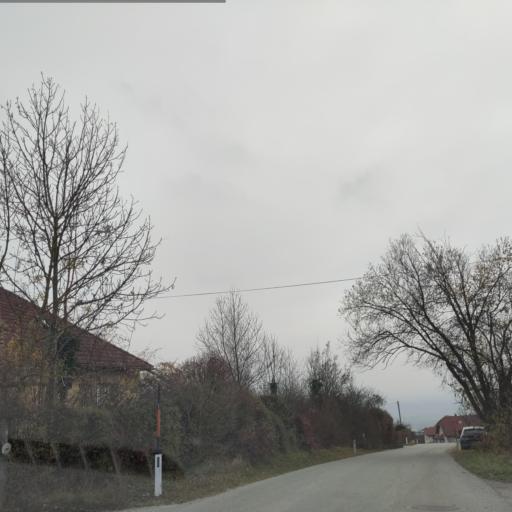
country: AT
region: Lower Austria
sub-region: Politischer Bezirk Sankt Polten
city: Neidling
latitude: 48.2444
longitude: 15.5274
